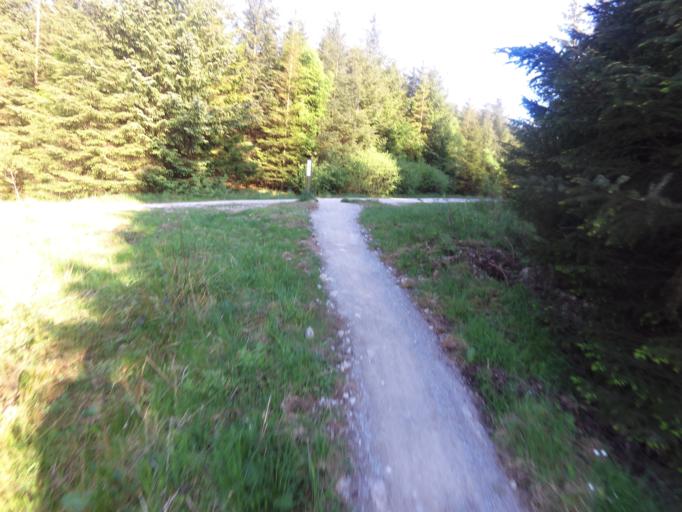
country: GB
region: England
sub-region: North Yorkshire
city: Settle
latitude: 54.0028
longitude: -2.3870
